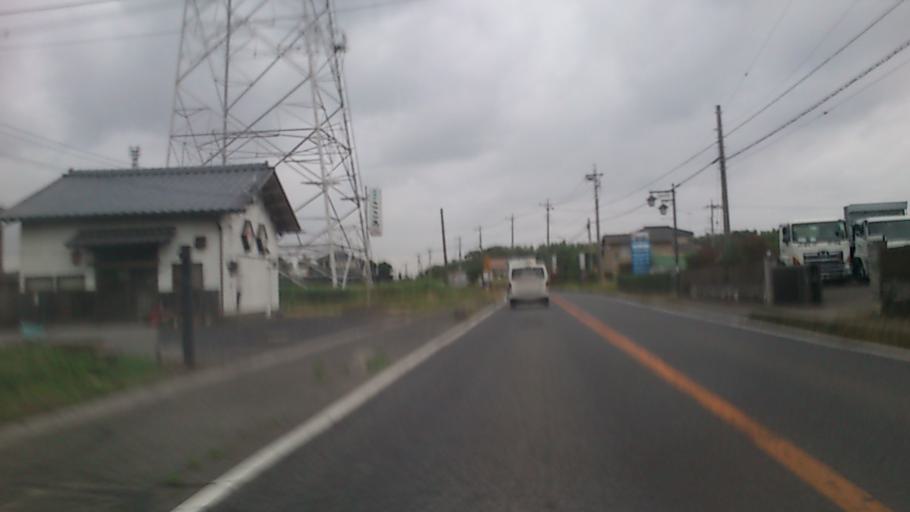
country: JP
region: Ibaraki
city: Sakai
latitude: 36.0983
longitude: 139.8382
